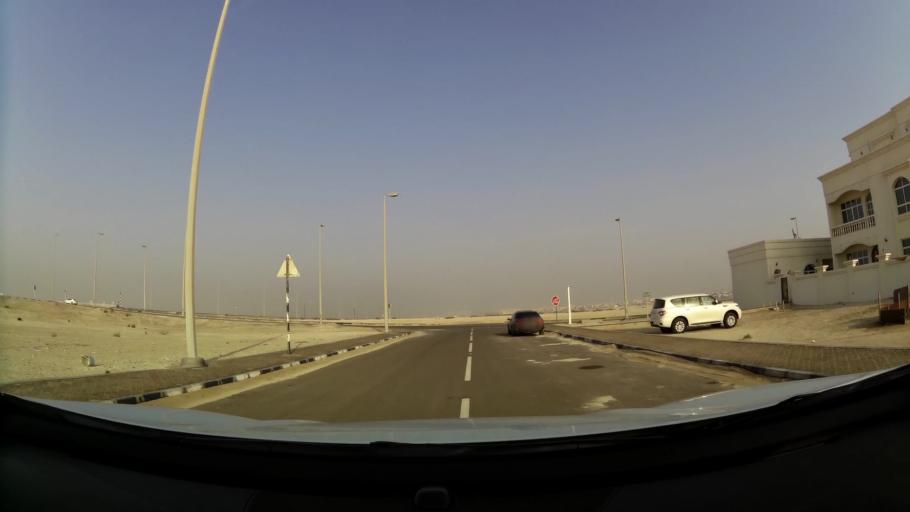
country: AE
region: Abu Dhabi
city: Abu Dhabi
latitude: 24.2780
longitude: 54.6407
